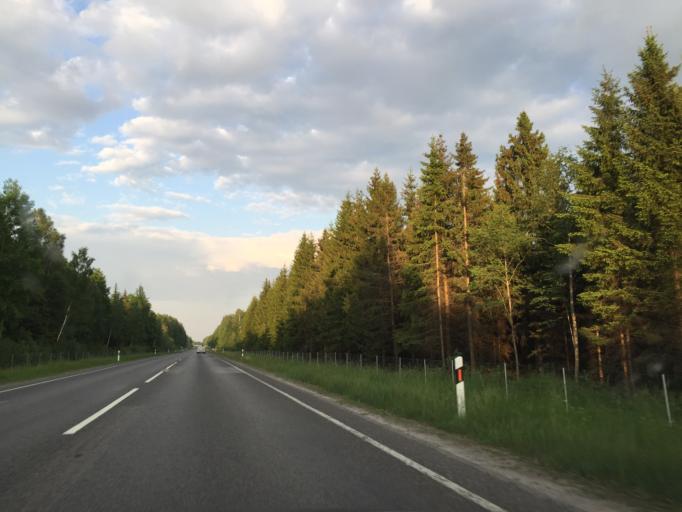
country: LT
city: Kursenai
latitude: 56.0006
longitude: 22.8070
